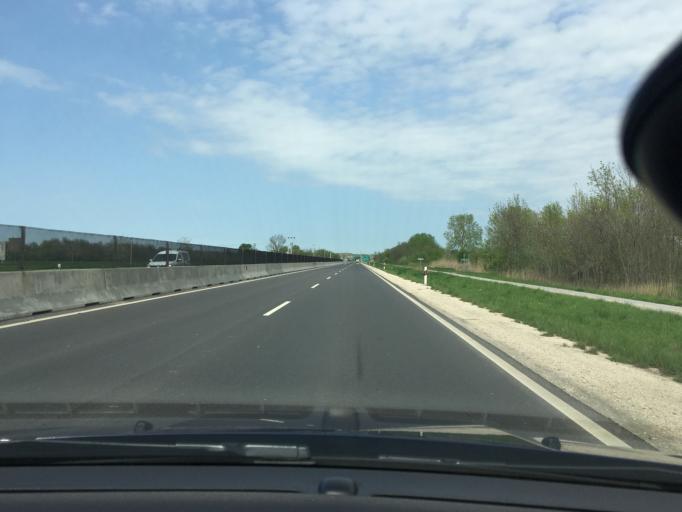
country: HU
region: Csongrad
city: Algyo
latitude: 46.3304
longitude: 20.1969
